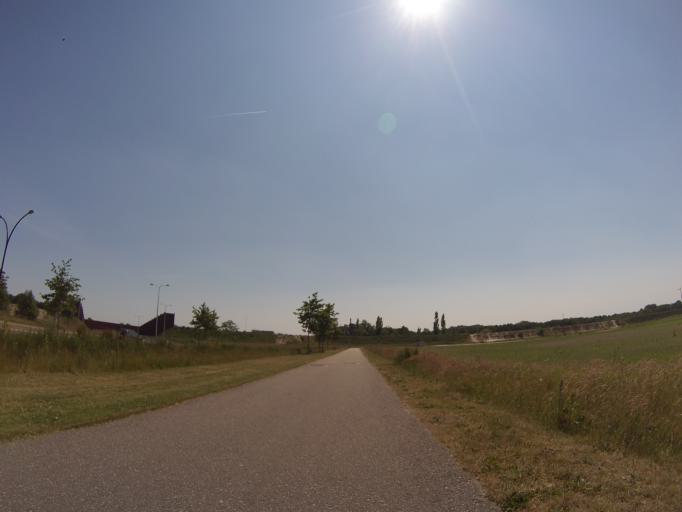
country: NL
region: Utrecht
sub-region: Gemeente Amersfoort
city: Randenbroek
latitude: 52.1814
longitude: 5.4309
